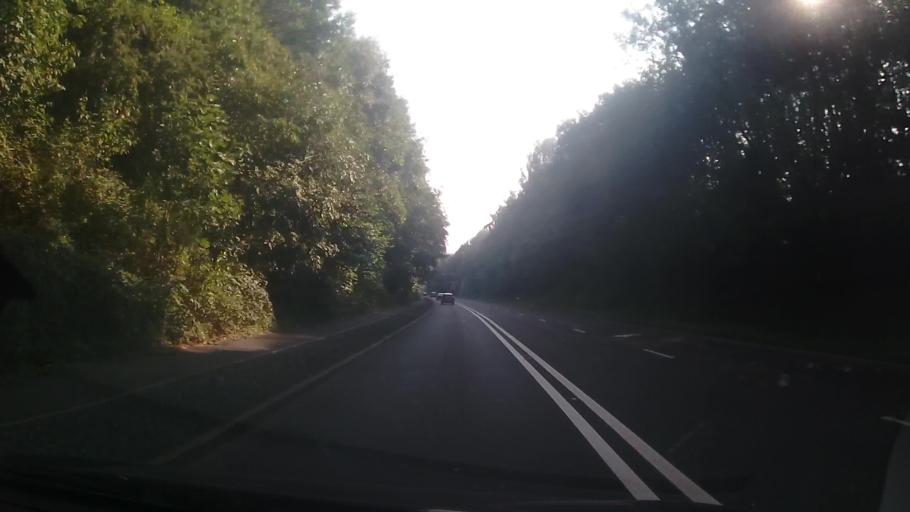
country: GB
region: England
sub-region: Shropshire
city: Bridgnorth
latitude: 52.5277
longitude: -2.4245
